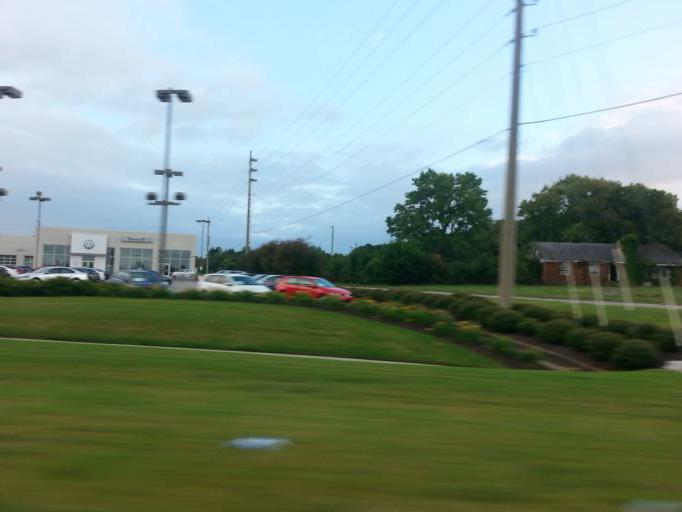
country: US
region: Alabama
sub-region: Madison County
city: Madison
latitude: 34.7486
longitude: -86.6931
